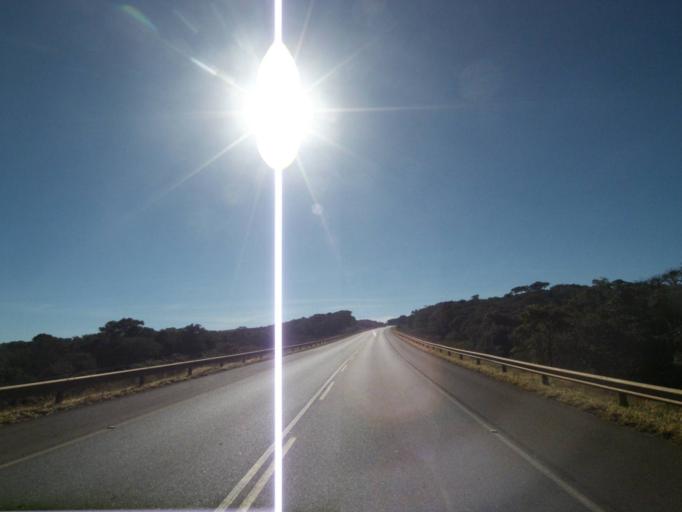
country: BR
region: Parana
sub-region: Tibagi
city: Tibagi
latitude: -24.4015
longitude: -50.3414
